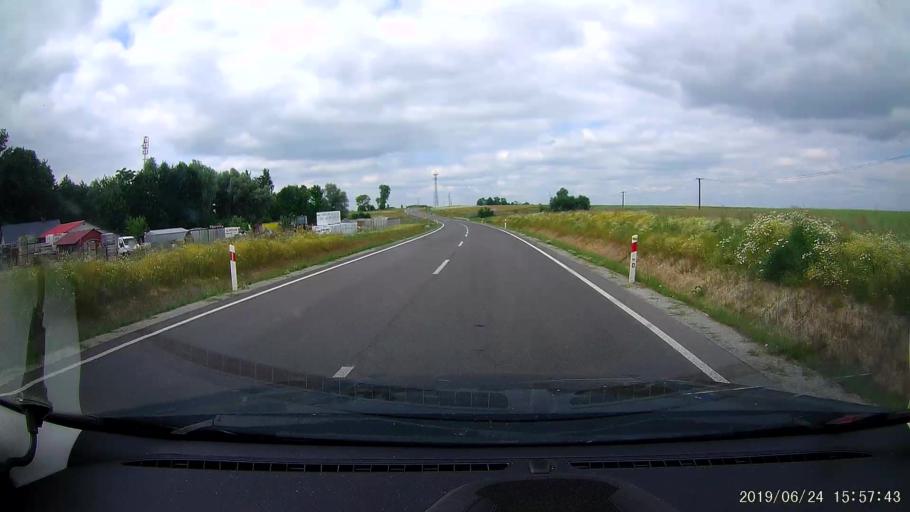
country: PL
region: Subcarpathian Voivodeship
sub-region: Powiat lubaczowski
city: Cieszanow
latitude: 50.2510
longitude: 23.1404
